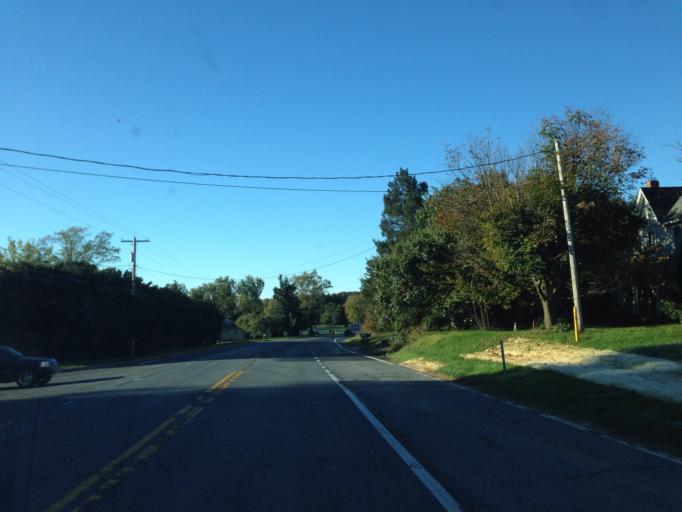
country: US
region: Maryland
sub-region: Carroll County
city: Mount Airy
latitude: 39.4453
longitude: -77.0948
